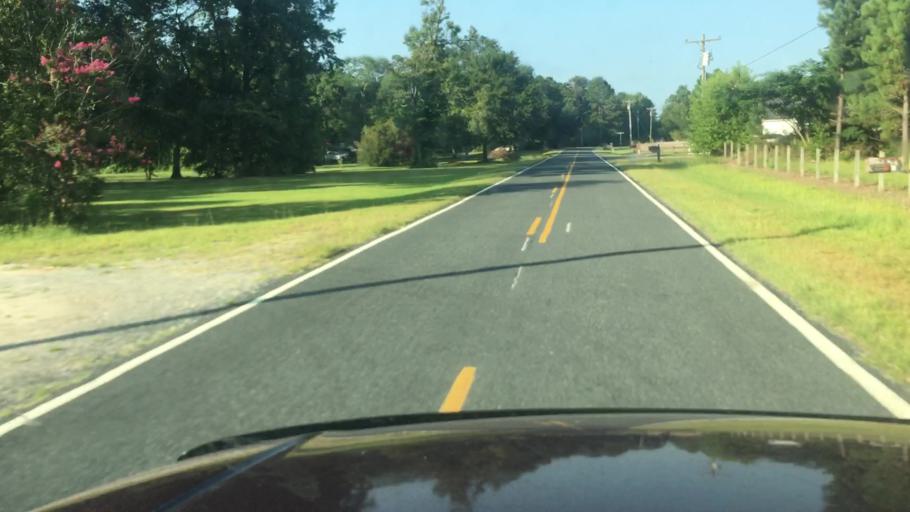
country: US
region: North Carolina
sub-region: Robeson County
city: Saint Pauls
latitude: 34.8432
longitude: -78.8881
